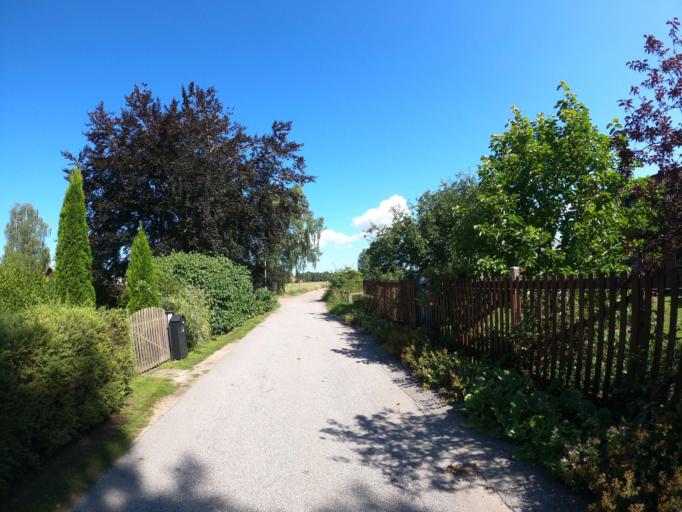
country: SE
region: Skane
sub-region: Lunds Kommun
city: Veberod
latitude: 55.6770
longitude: 13.4250
